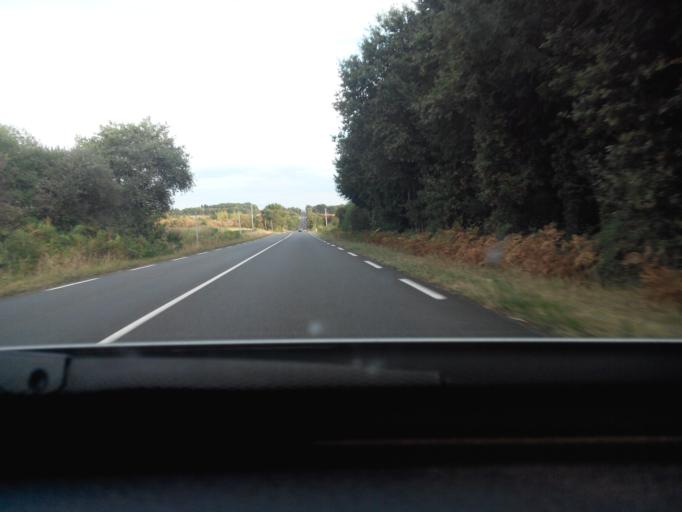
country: FR
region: Poitou-Charentes
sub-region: Departement de la Charente
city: Etagnac
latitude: 45.9106
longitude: 0.7530
